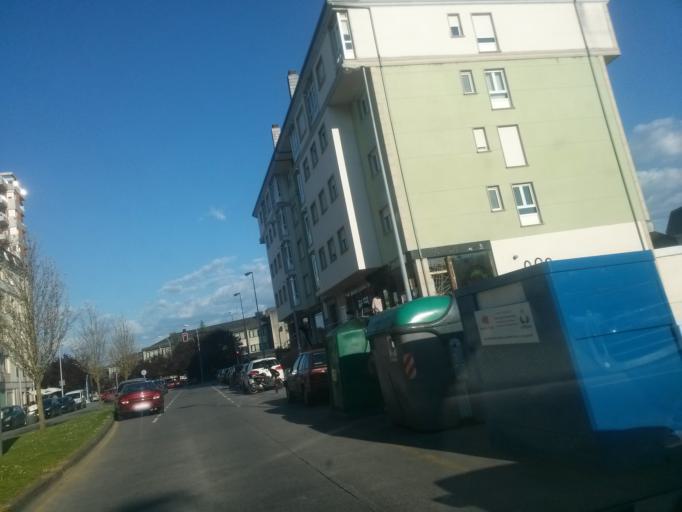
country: ES
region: Galicia
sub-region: Provincia de Lugo
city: Lugo
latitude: 42.9948
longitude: -7.5510
